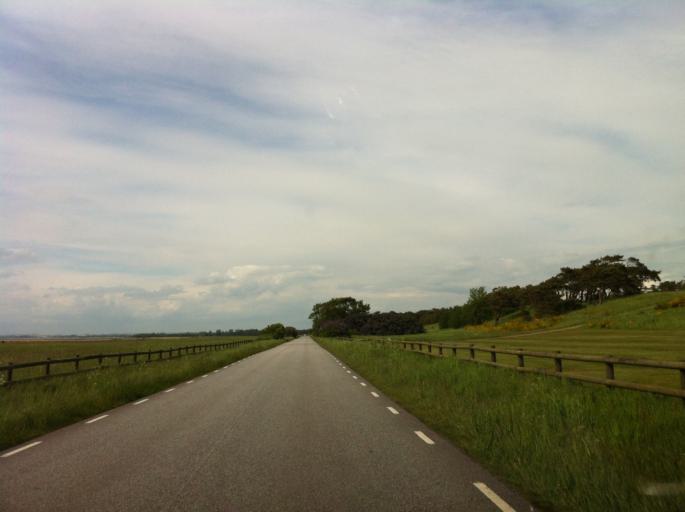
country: SE
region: Skane
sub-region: Kavlinge Kommun
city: Hofterup
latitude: 55.7919
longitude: 12.9384
